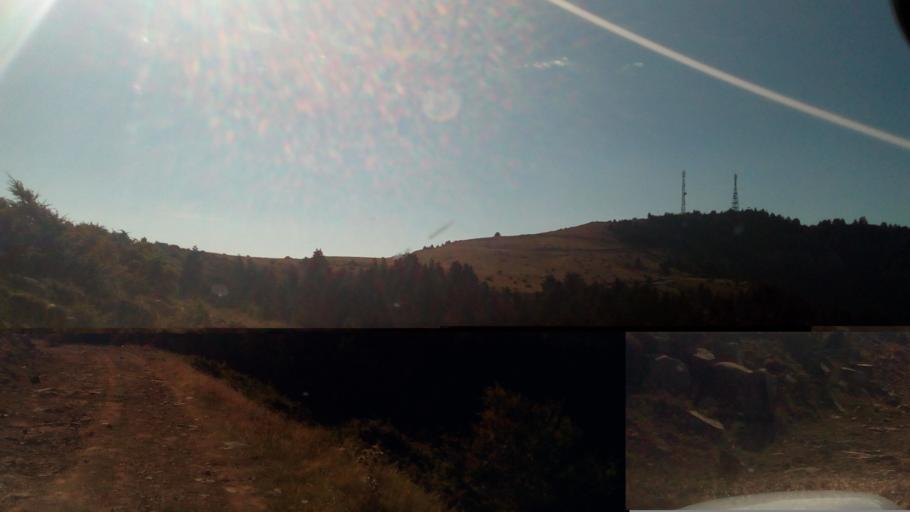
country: GR
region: Central Greece
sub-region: Nomos Fokidos
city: Lidoriki
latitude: 38.6103
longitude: 21.9638
